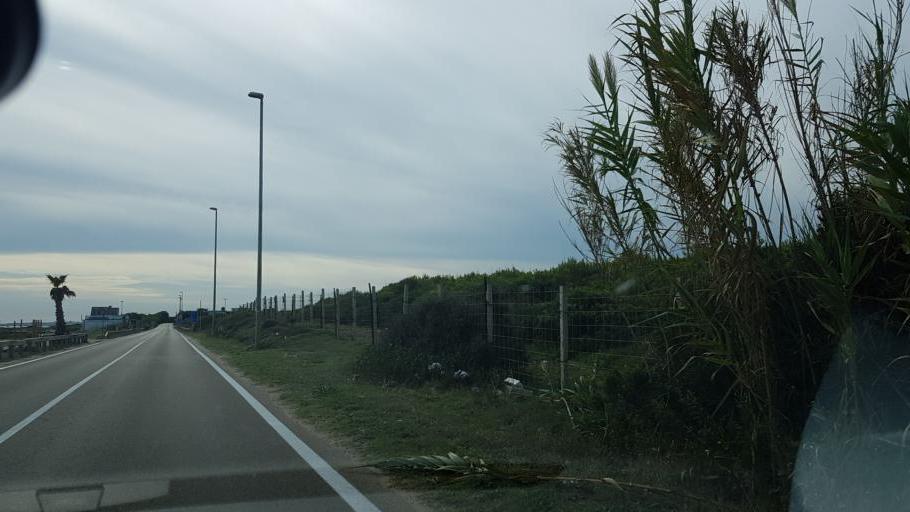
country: IT
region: Apulia
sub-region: Provincia di Lecce
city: Melendugno
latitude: 40.3315
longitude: 18.3714
